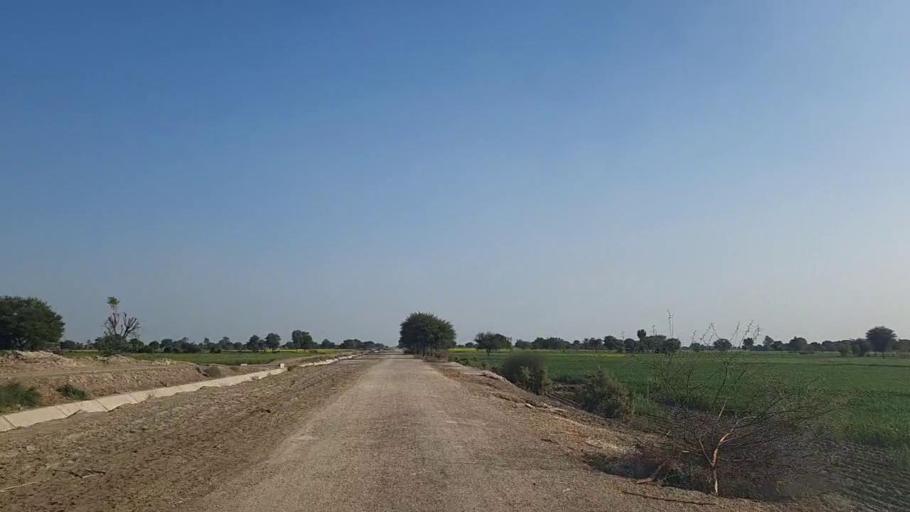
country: PK
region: Sindh
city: Shahpur Chakar
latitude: 26.2043
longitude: 68.6446
